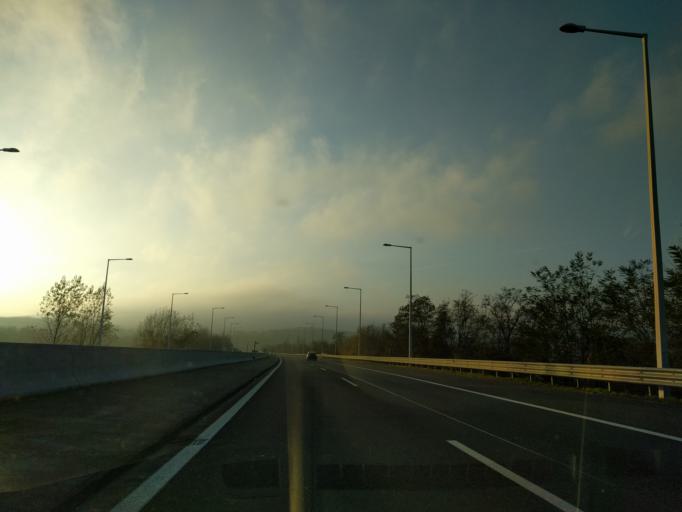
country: AT
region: Lower Austria
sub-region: Politischer Bezirk Wien-Umgebung
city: Purkersdorf
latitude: 48.2048
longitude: 16.2283
